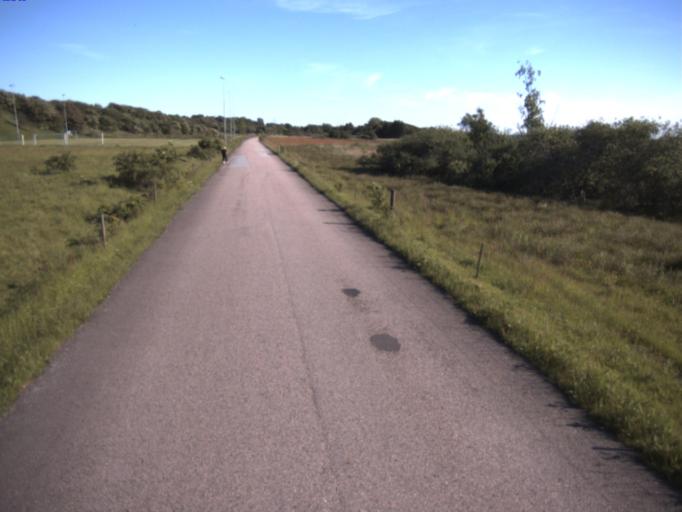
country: SE
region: Skane
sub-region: Helsingborg
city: Rydeback
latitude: 55.9875
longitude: 12.7559
